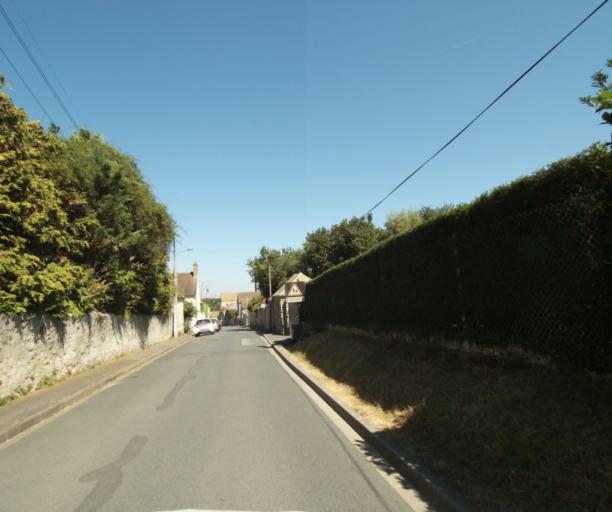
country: FR
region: Ile-de-France
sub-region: Departement de l'Essonne
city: Itteville
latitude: 48.5133
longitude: 2.3430
